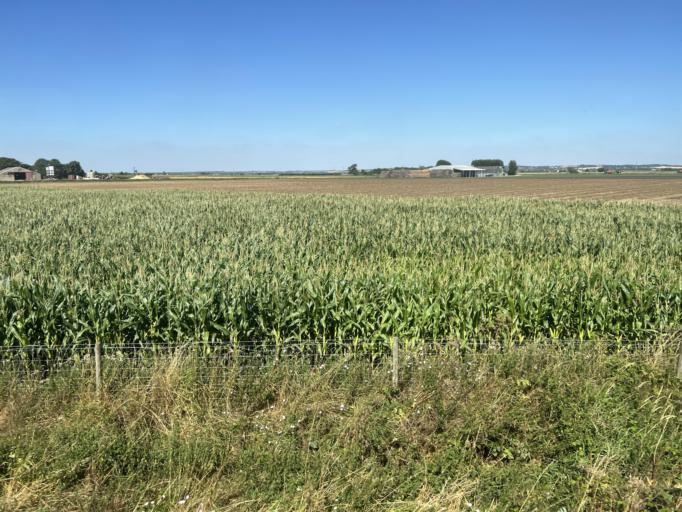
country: GB
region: England
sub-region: Lincolnshire
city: Spilsby
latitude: 53.1046
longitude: 0.1160
